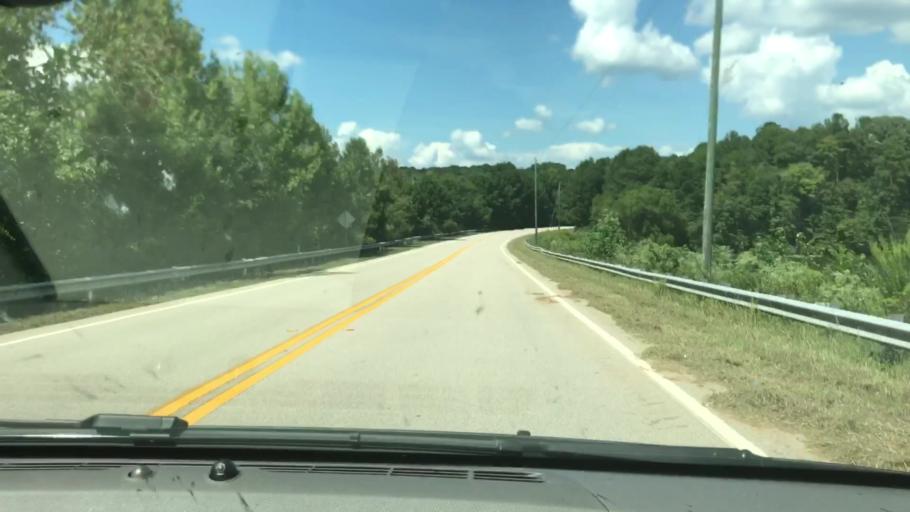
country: US
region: Georgia
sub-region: Troup County
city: La Grange
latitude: 33.1342
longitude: -85.0897
